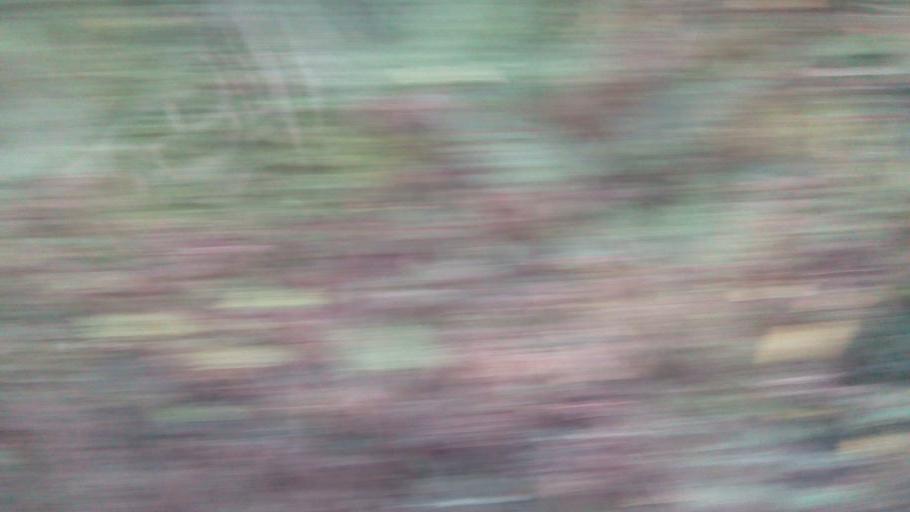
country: TW
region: Taiwan
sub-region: Hualien
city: Hualian
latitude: 24.3485
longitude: 121.3177
